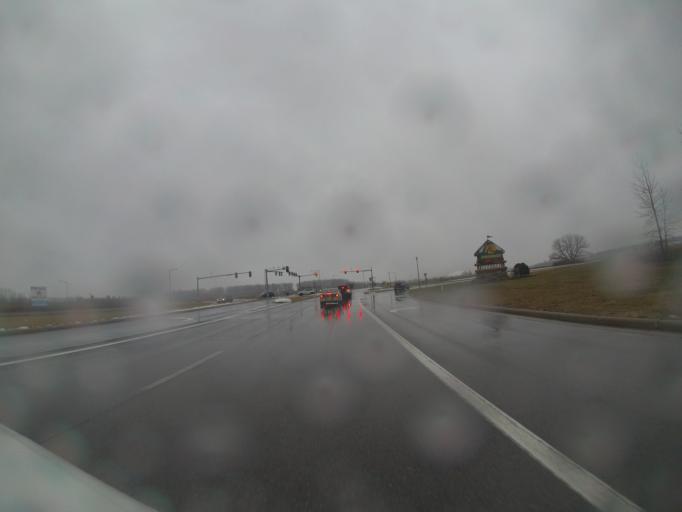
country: US
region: Ohio
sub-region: Wood County
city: Perrysburg
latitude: 41.5593
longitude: -83.5792
